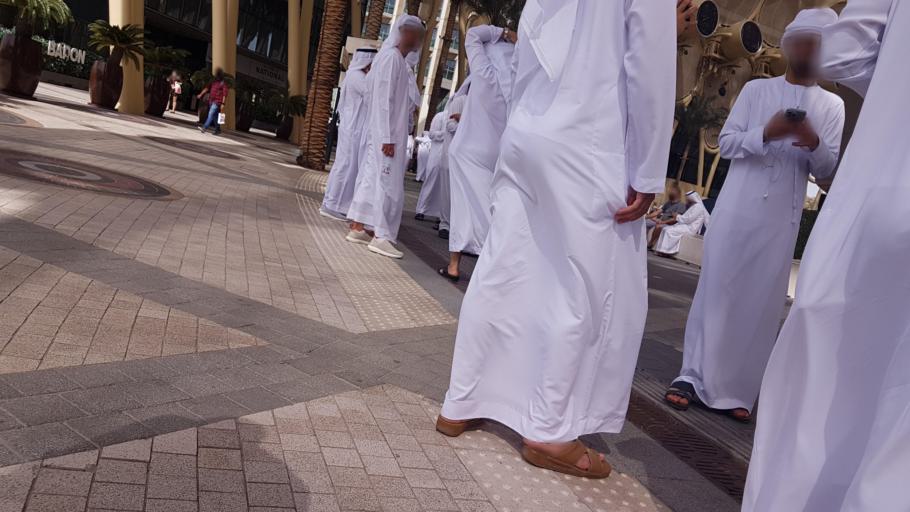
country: AE
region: Dubai
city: Dubai
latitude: 24.9603
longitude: 55.1508
